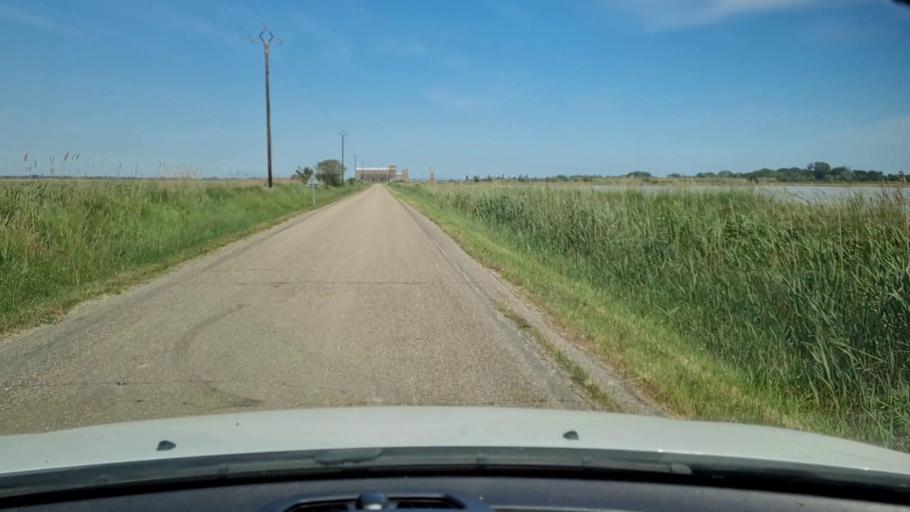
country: FR
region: Languedoc-Roussillon
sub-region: Departement du Gard
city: Saint-Gilles
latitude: 43.5799
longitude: 4.4004
